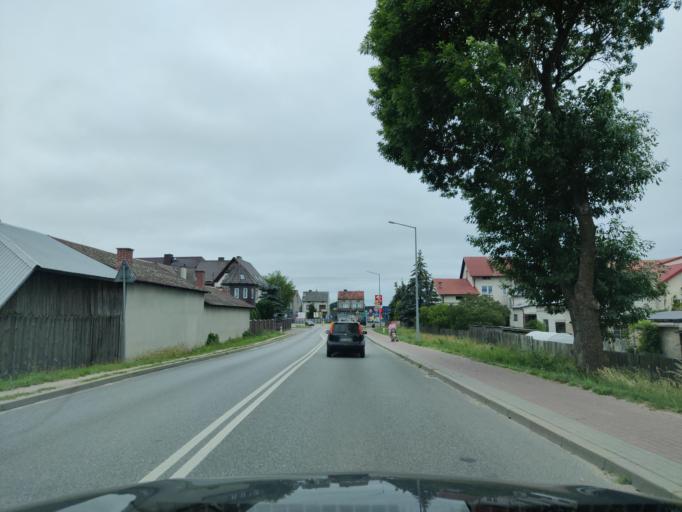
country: PL
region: Masovian Voivodeship
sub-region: Powiat ostrolecki
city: Myszyniec
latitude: 53.3865
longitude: 21.3404
